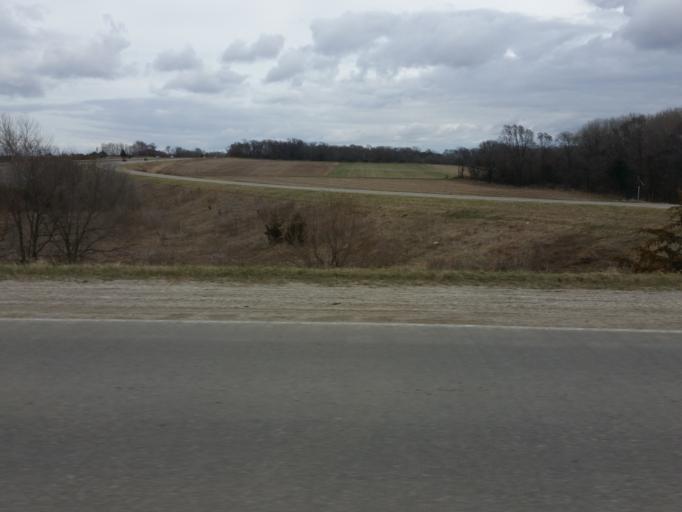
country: US
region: Iowa
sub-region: Black Hawk County
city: Elk Run Heights
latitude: 42.4481
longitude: -92.2196
